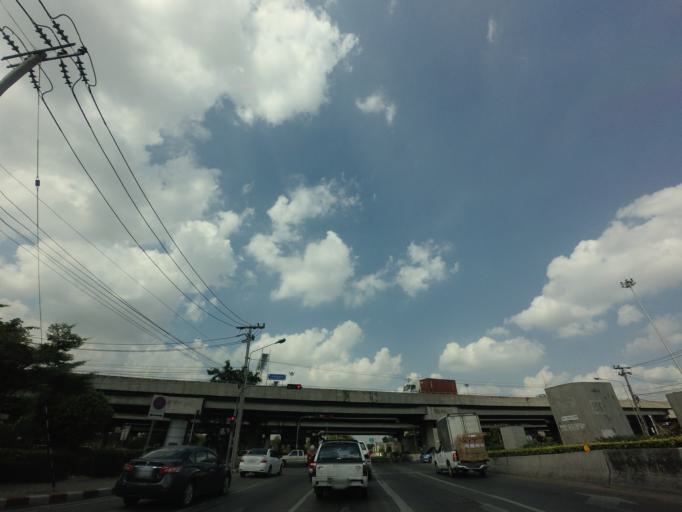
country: TH
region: Bangkok
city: Lat Phrao
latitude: 13.8250
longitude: 100.6287
